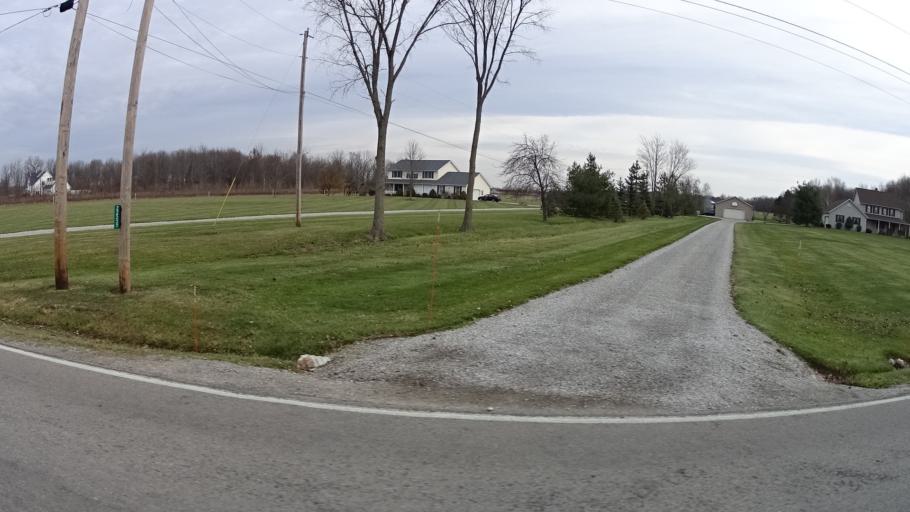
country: US
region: Ohio
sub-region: Lorain County
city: Lagrange
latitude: 41.1601
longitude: -82.0912
